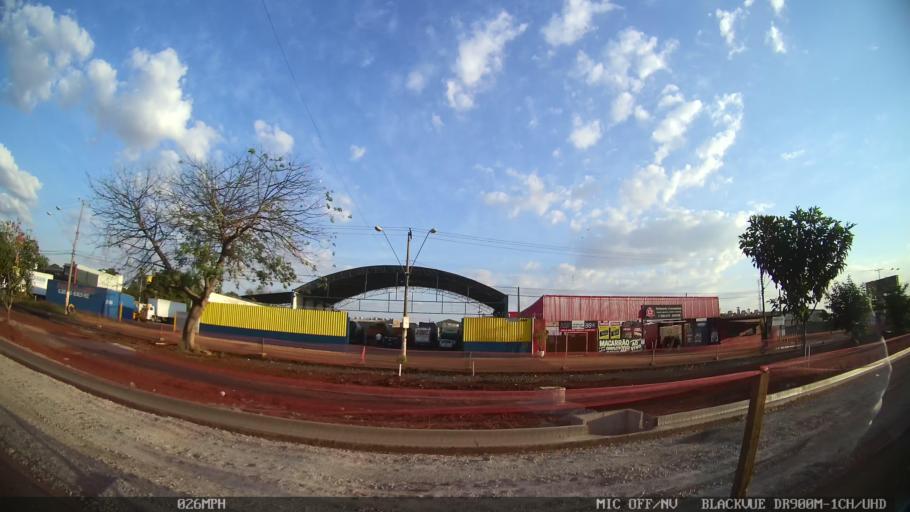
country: BR
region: Sao Paulo
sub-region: Ribeirao Preto
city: Ribeirao Preto
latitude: -21.1410
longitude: -47.7843
